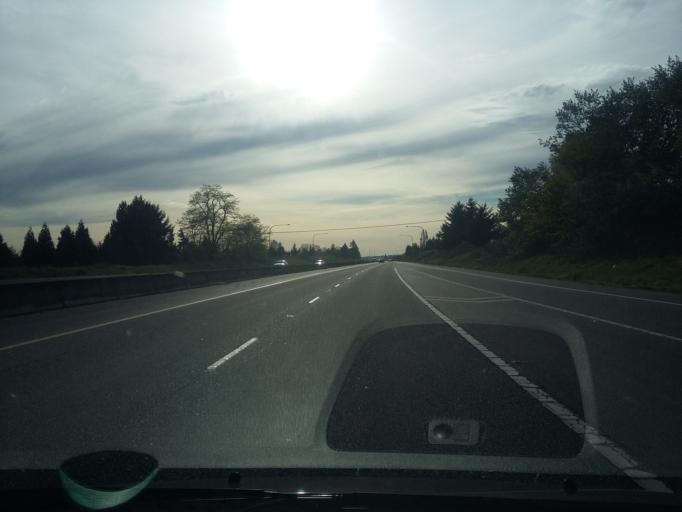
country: US
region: Washington
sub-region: Clark County
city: Walnut Grove
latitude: 45.6481
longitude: -122.6067
